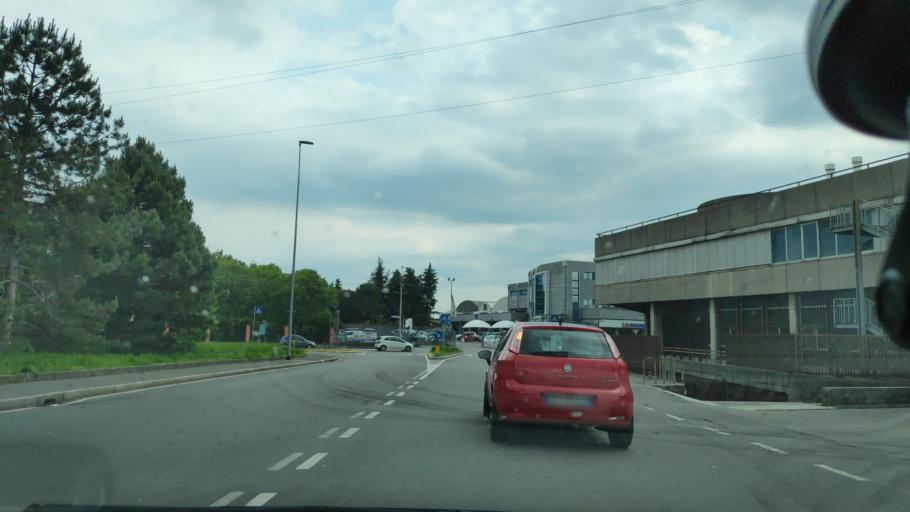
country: IT
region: Lombardy
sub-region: Provincia di Bergamo
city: Orio al Serio
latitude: 45.6788
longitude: 9.6749
